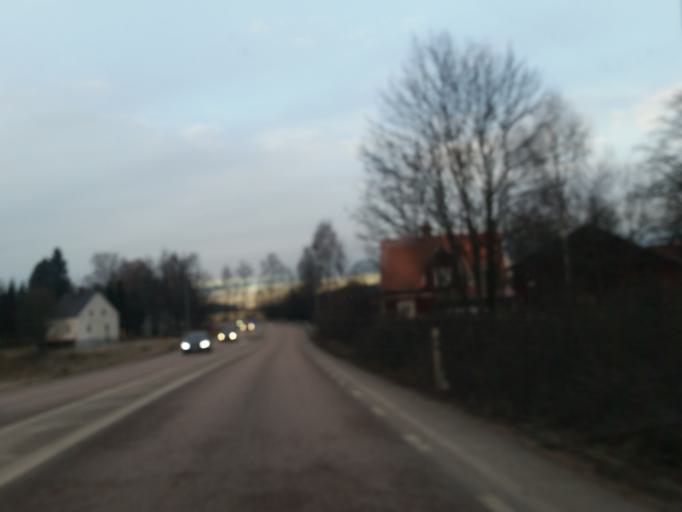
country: SE
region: Dalarna
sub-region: Leksand Municipality
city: Smedby
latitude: 60.6803
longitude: 15.0823
